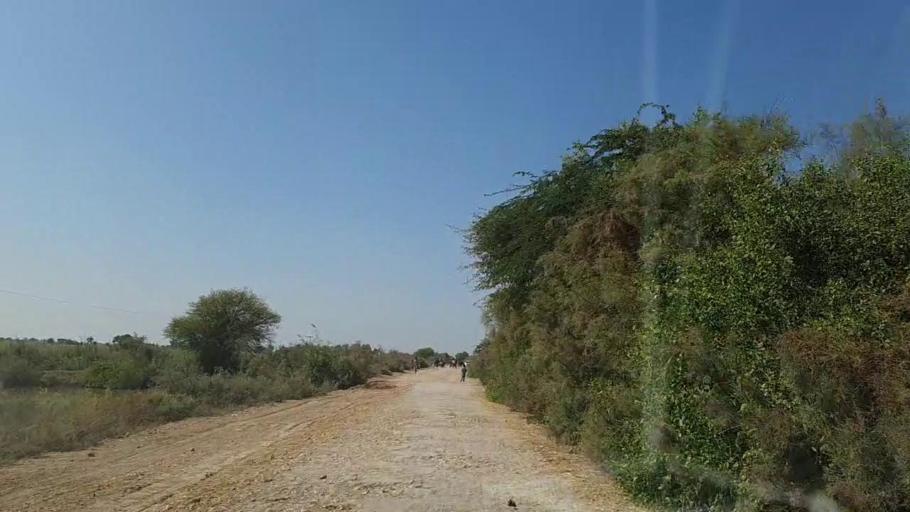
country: PK
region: Sindh
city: Chuhar Jamali
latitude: 24.4182
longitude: 68.0230
